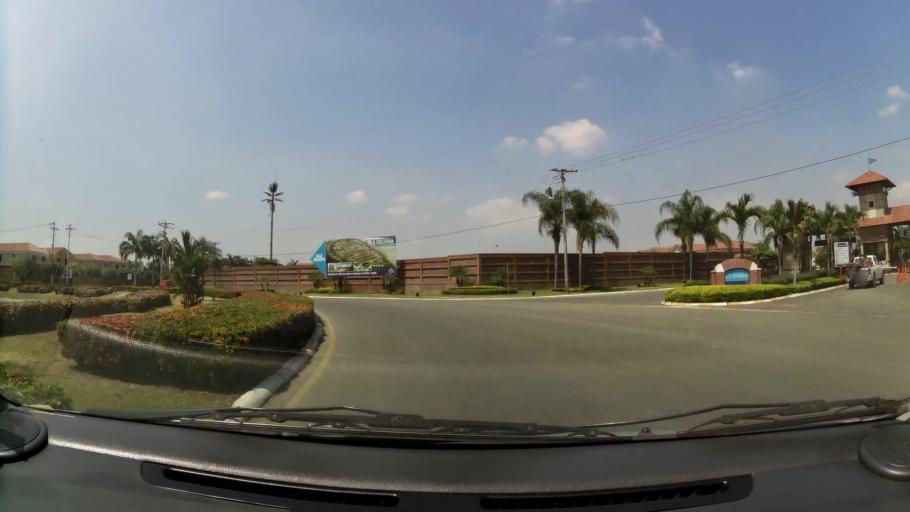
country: EC
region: Guayas
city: Eloy Alfaro
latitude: -2.0727
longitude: -79.8417
